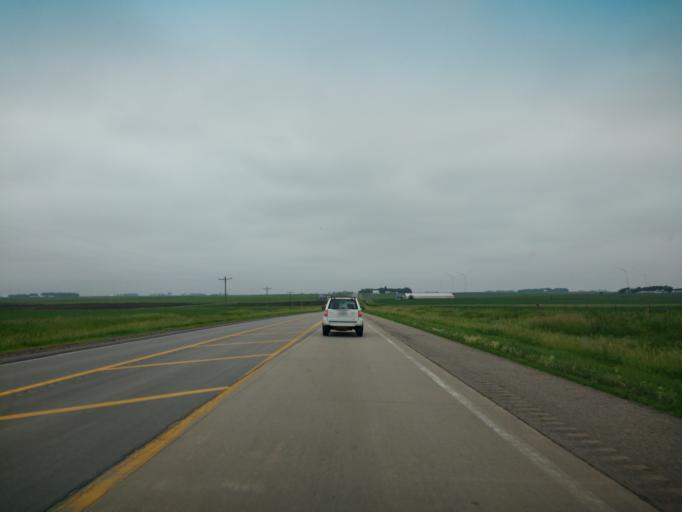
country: US
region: Iowa
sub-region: O'Brien County
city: Hartley
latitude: 43.1850
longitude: -95.5077
